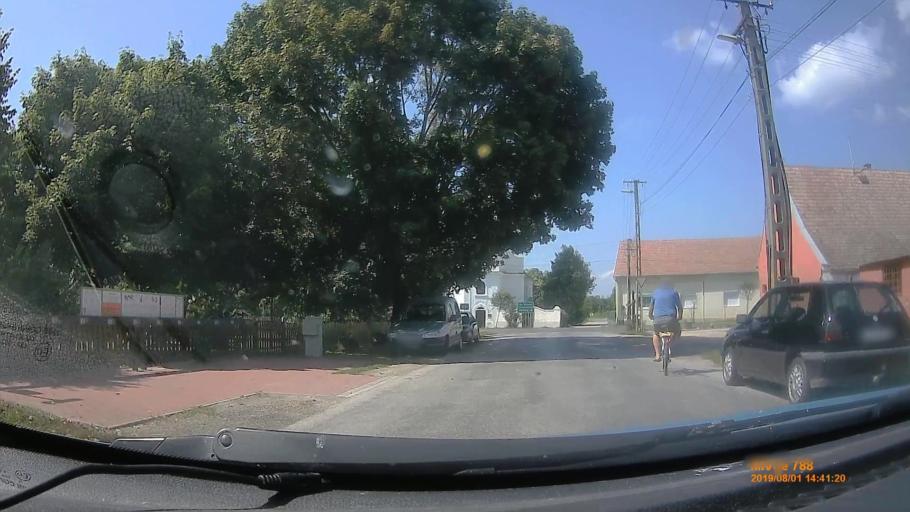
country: HR
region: Osjecko-Baranjska
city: Viljevo
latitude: 45.8241
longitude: 18.1014
